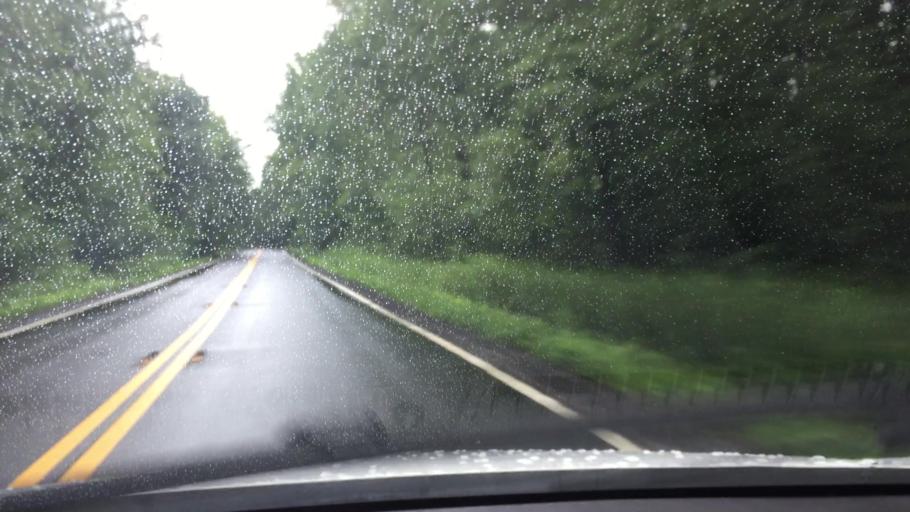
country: US
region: Massachusetts
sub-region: Berkshire County
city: Hinsdale
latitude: 42.3976
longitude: -73.1685
